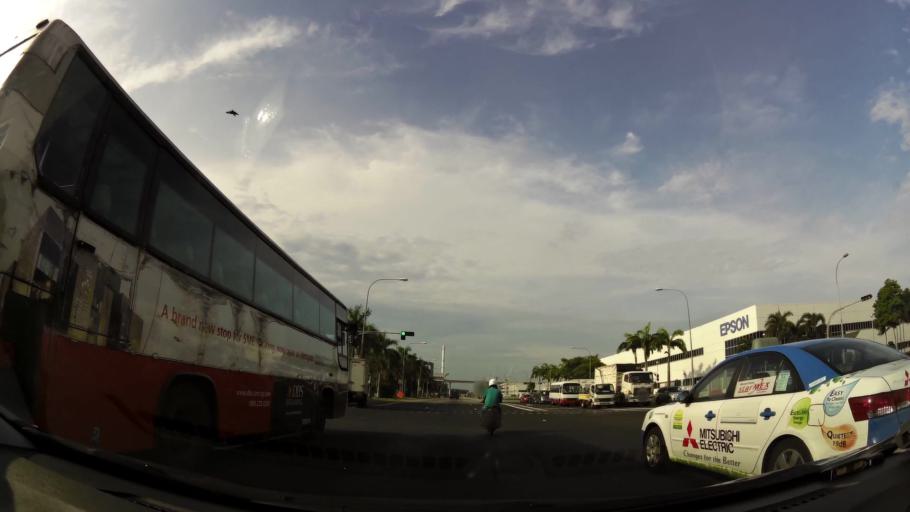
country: MY
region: Johor
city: Johor Bahru
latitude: 1.3347
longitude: 103.6427
